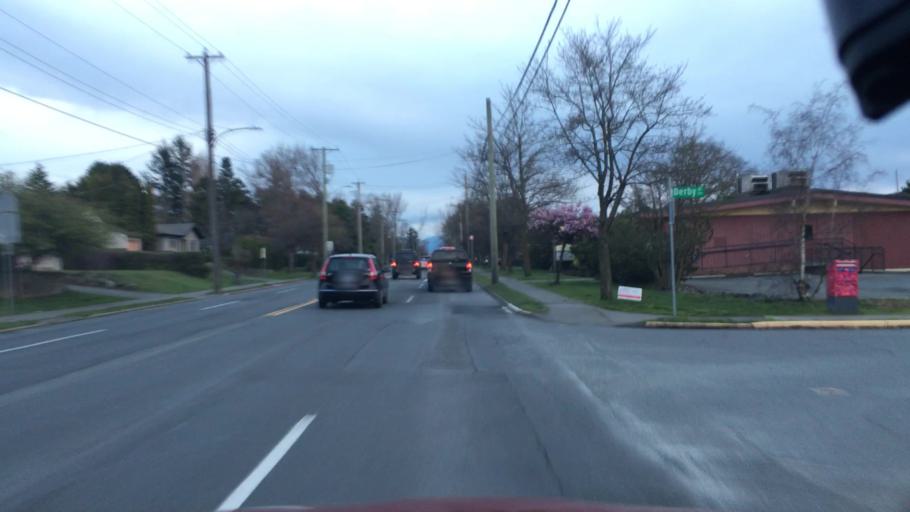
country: CA
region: British Columbia
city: Oak Bay
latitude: 48.4552
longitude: -123.3332
